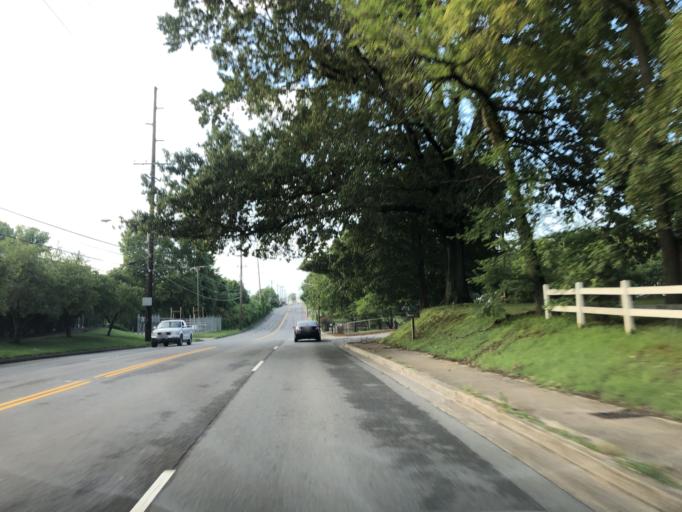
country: US
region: Tennessee
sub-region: Davidson County
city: Nashville
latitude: 36.1484
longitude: -86.7221
